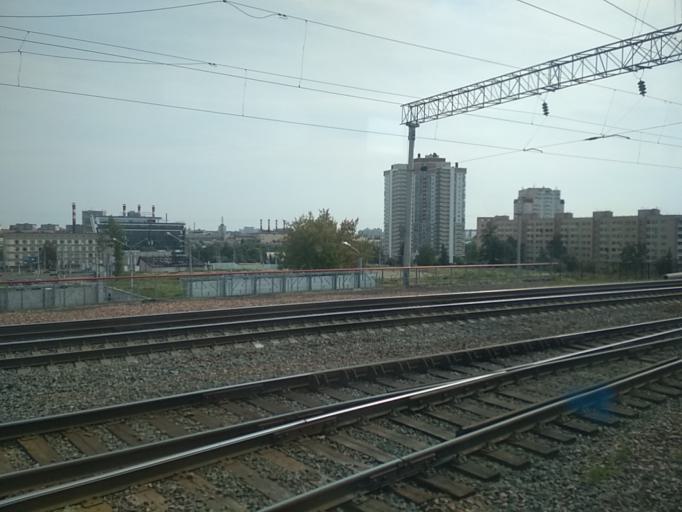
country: BY
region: Minsk
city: Minsk
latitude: 53.8856
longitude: 27.5630
